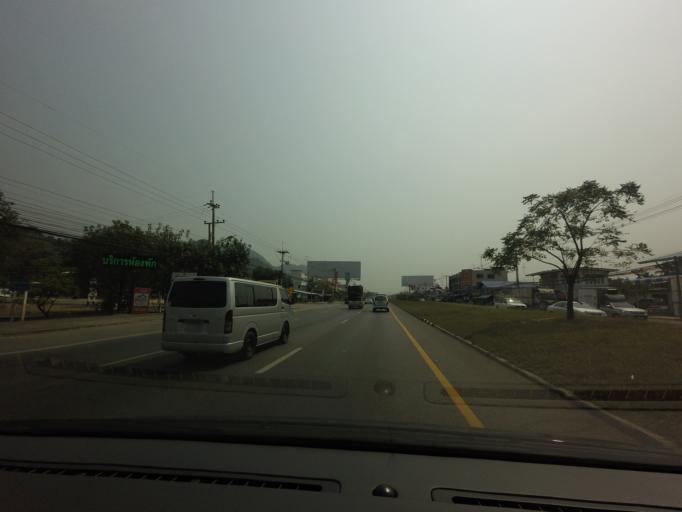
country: TH
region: Phetchaburi
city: Cha-am
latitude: 12.8385
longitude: 99.9315
